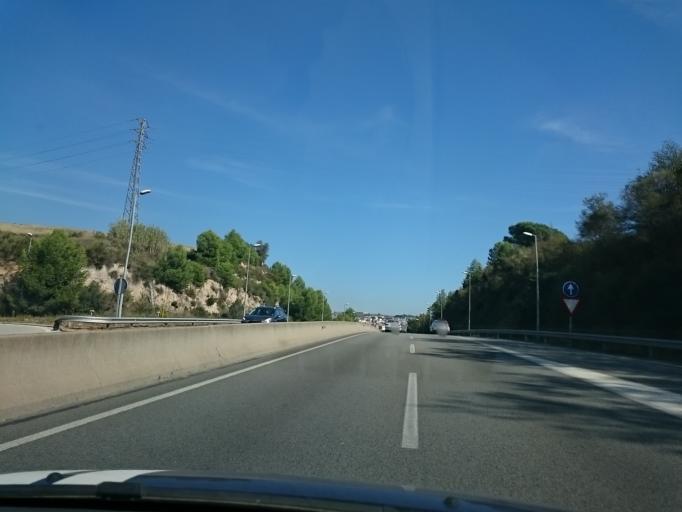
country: ES
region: Catalonia
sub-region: Provincia de Barcelona
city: Granollers
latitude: 41.5959
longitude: 2.2691
